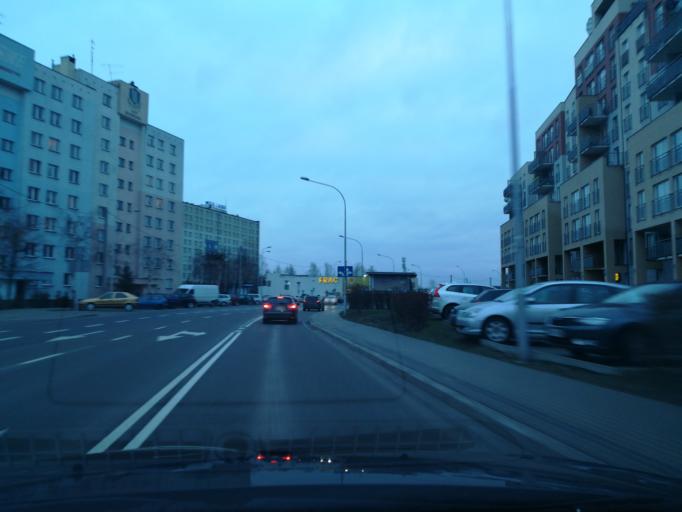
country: PL
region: Subcarpathian Voivodeship
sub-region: Rzeszow
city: Rzeszow
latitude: 50.0187
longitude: 22.0040
